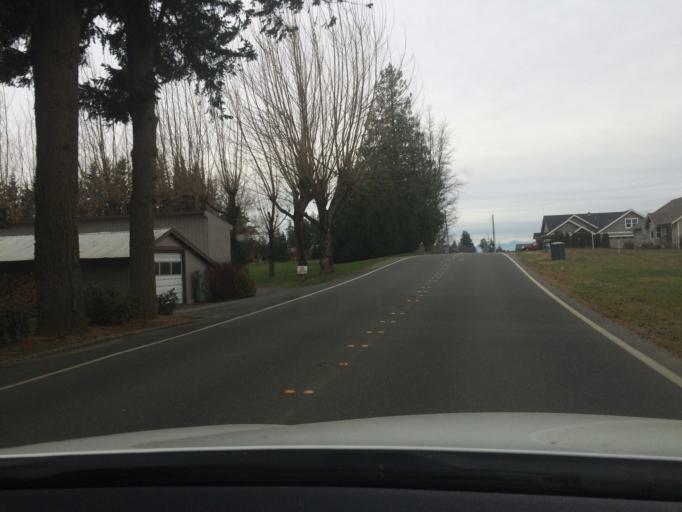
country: US
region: Washington
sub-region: Whatcom County
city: Lynden
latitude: 48.9572
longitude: -122.4188
